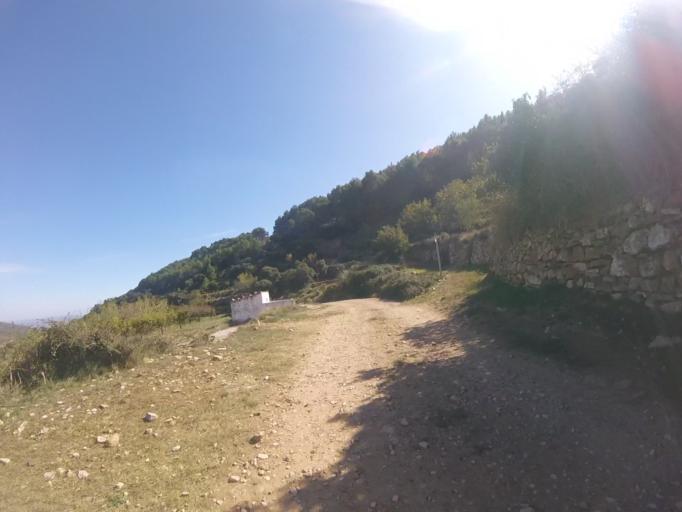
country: ES
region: Valencia
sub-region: Provincia de Castello
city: Sierra-Engarceran
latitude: 40.2728
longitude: -0.0043
